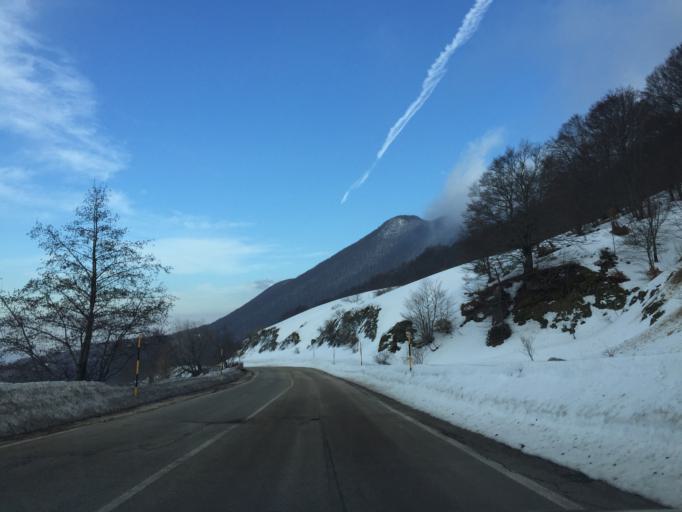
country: IT
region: Molise
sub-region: Provincia di Campobasso
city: San Massimo
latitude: 41.4654
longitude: 14.4116
